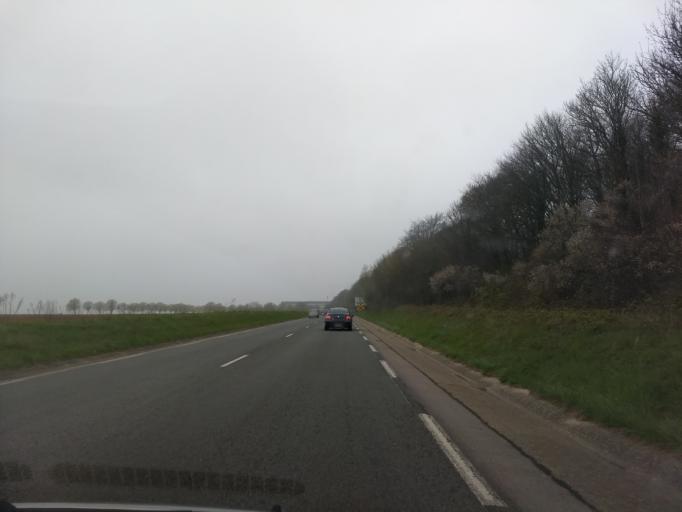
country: FR
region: Nord-Pas-de-Calais
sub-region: Departement du Pas-de-Calais
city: Verton
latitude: 50.4139
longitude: 1.6727
